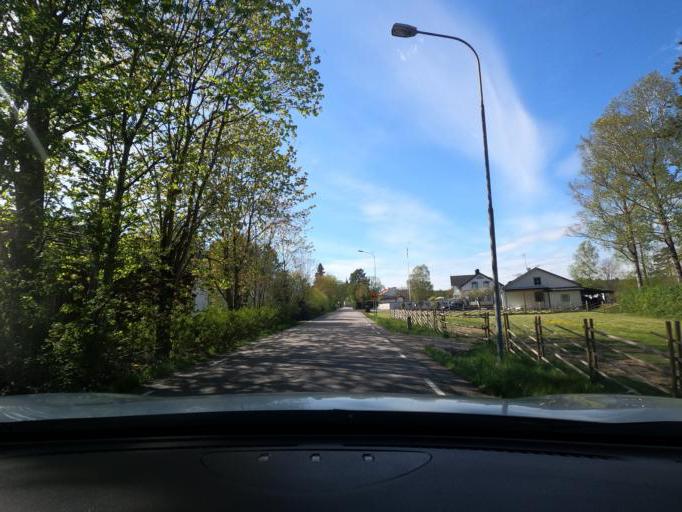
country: SE
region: Vaestra Goetaland
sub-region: Harryda Kommun
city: Ravlanda
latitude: 57.6475
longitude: 12.4938
